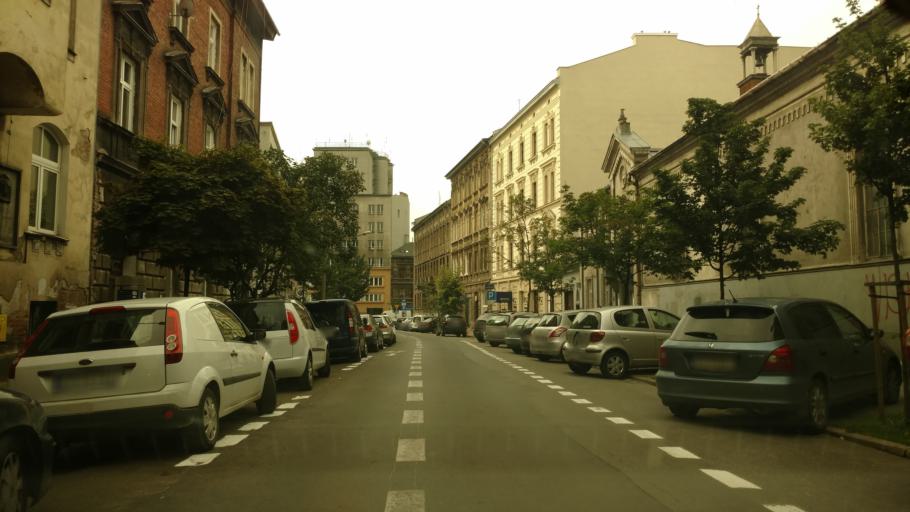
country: PL
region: Lesser Poland Voivodeship
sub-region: Krakow
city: Krakow
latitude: 50.0671
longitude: 19.9341
